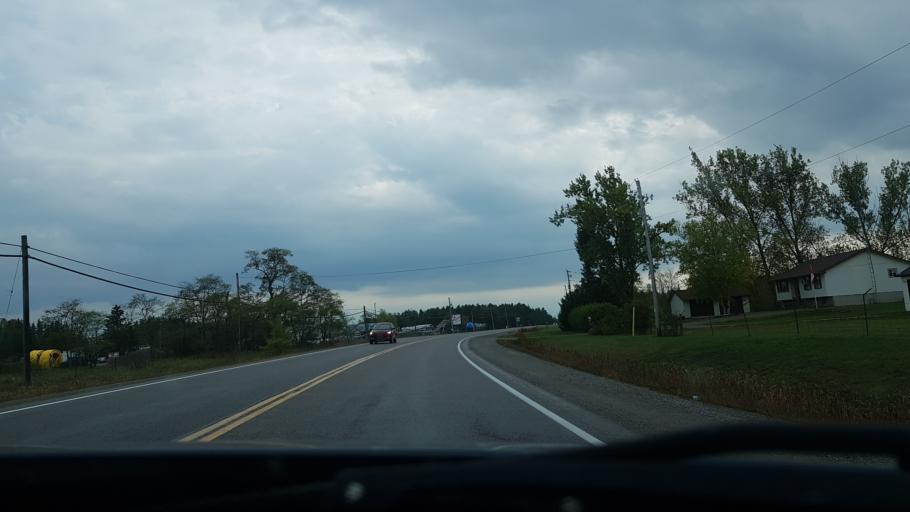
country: CA
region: Ontario
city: Omemee
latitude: 44.4324
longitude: -78.7776
